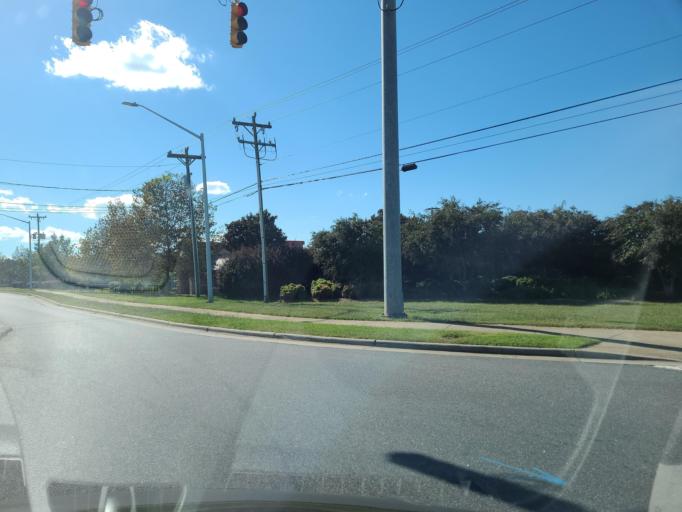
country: US
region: North Carolina
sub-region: Catawba County
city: Conover
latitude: 35.7261
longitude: -81.2074
